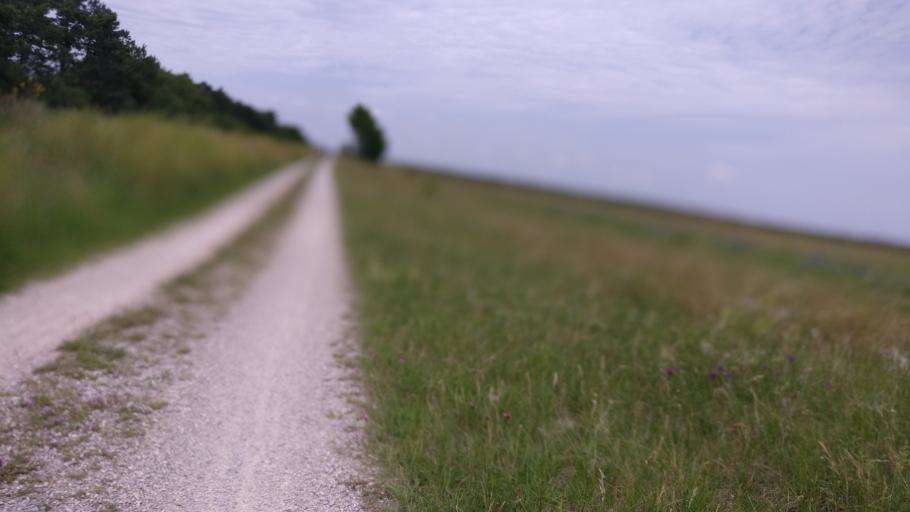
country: AT
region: Lower Austria
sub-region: Politischer Bezirk Wiener Neustadt
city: Sollenau
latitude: 47.8689
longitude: 16.2816
